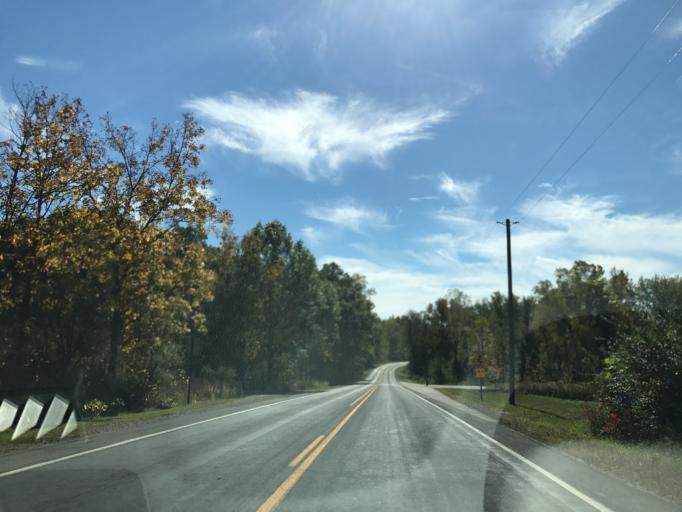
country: US
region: Michigan
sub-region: Washtenaw County
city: Ann Arbor
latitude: 42.3417
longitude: -83.6620
